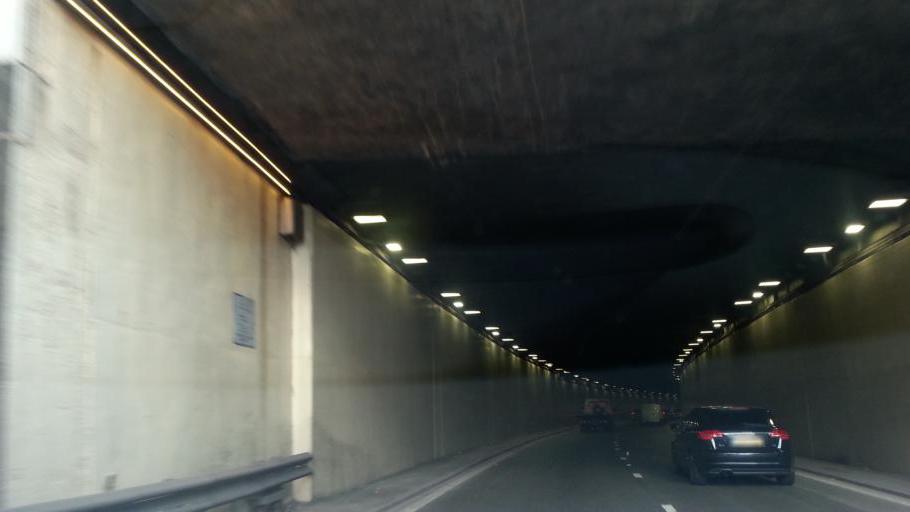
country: GB
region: England
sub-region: City and Borough of Leeds
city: Leeds
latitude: 53.8014
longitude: -1.5547
